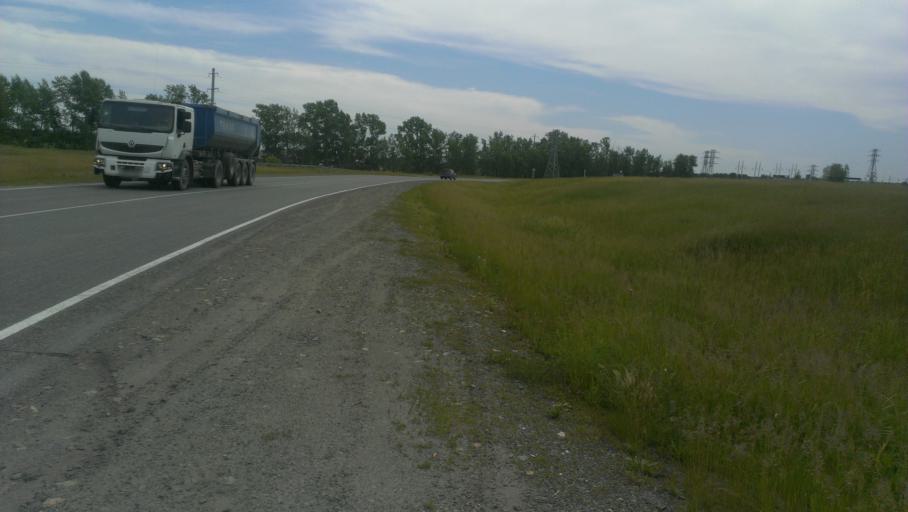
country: RU
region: Altai Krai
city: Sannikovo
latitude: 53.3403
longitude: 83.9371
